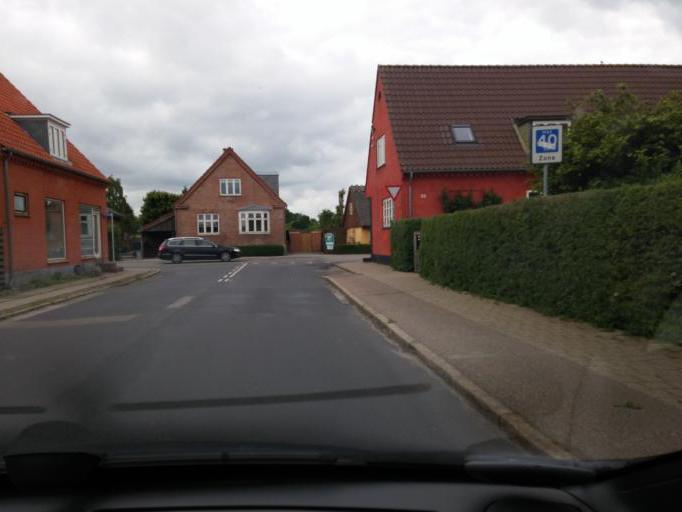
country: DK
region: Capital Region
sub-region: Hillerod Kommune
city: Hillerod
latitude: 55.9363
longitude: 12.3182
